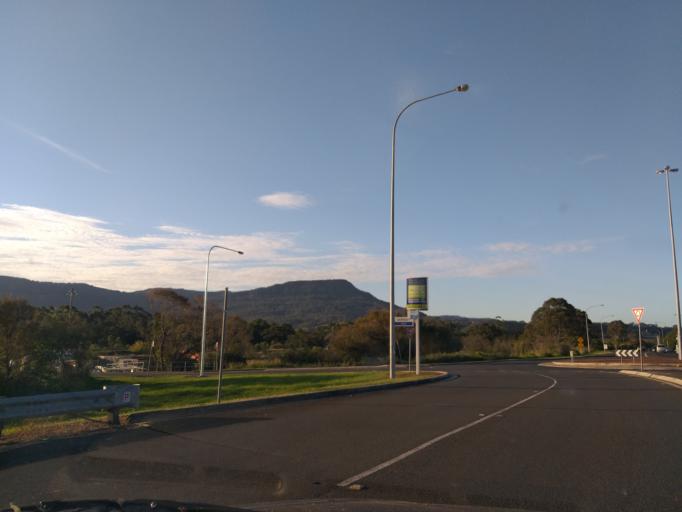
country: AU
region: New South Wales
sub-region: Wollongong
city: Koonawarra
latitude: -34.4835
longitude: 150.8018
